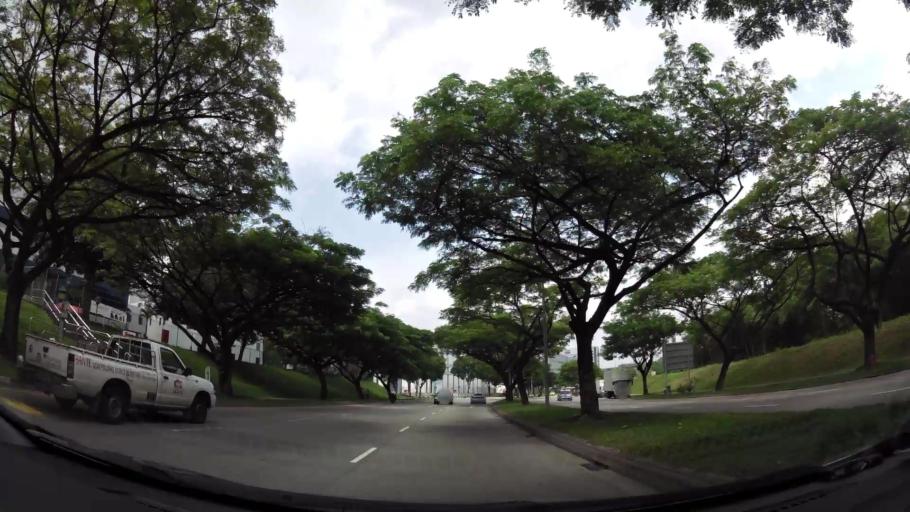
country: SG
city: Singapore
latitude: 1.3709
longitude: 103.9304
